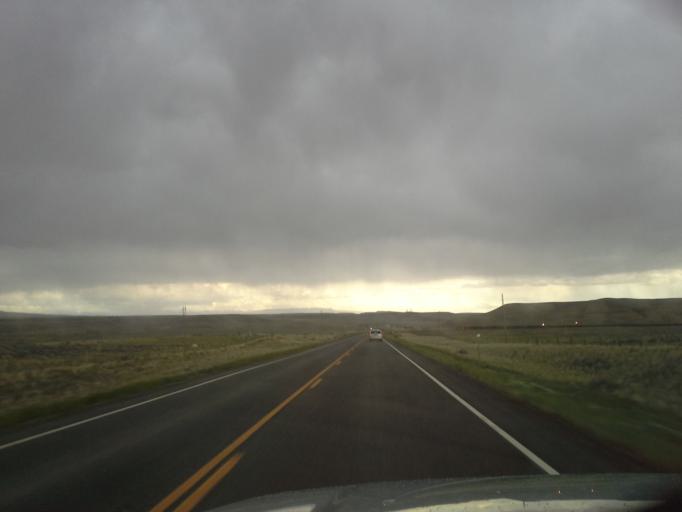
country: US
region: Wyoming
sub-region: Park County
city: Powell
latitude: 45.0685
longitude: -108.6768
